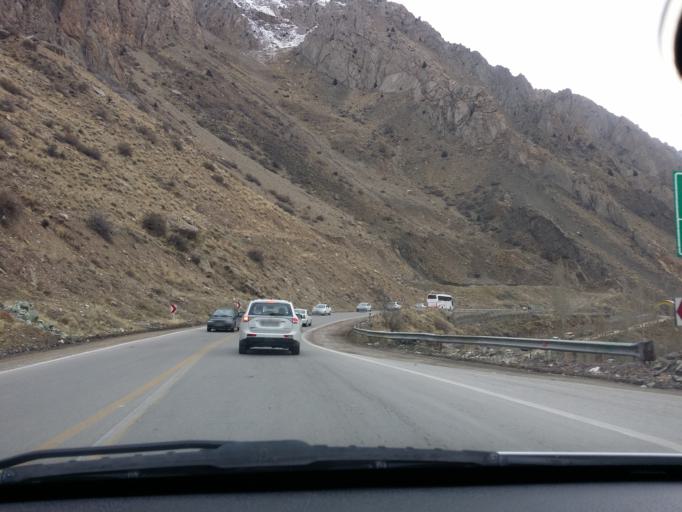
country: IR
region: Tehran
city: Tajrish
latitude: 36.0702
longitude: 51.3096
